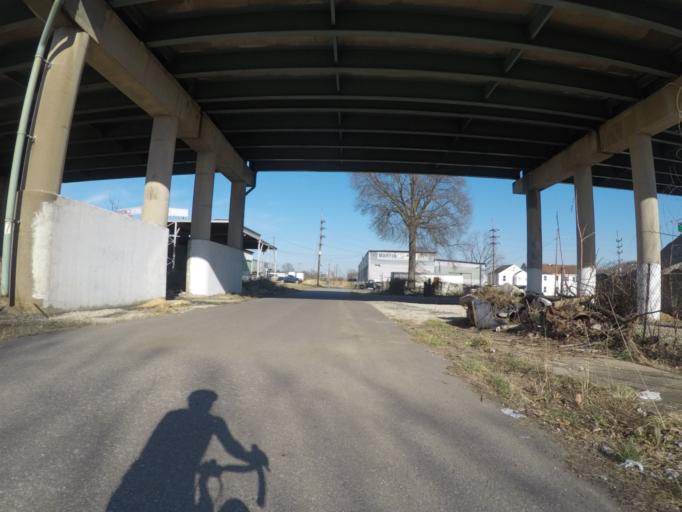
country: US
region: West Virginia
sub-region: Cabell County
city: Huntington
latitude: 38.4099
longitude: -82.4834
